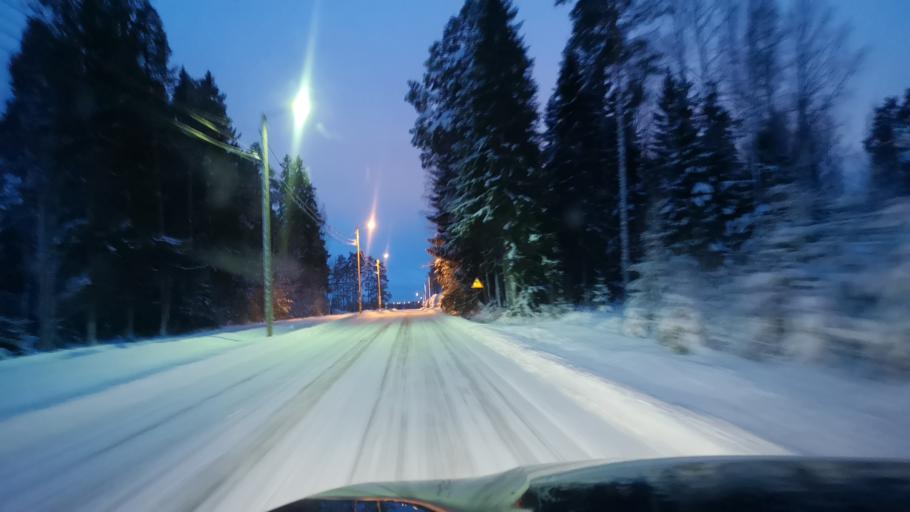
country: FI
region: Varsinais-Suomi
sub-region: Loimaa
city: Loimaa
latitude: 60.8658
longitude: 23.0844
